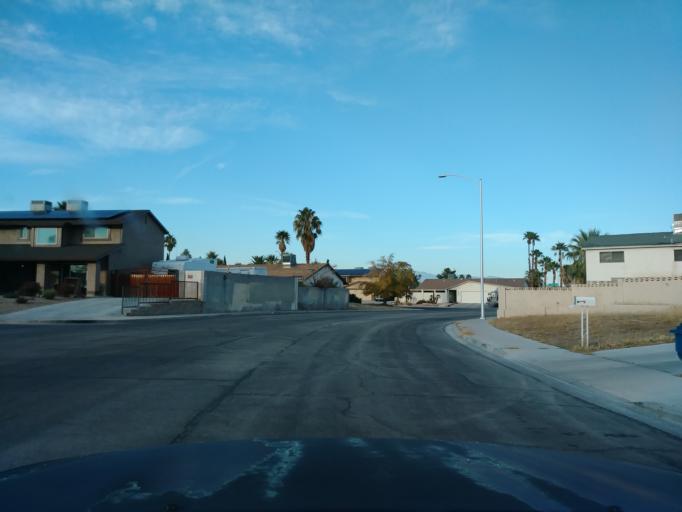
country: US
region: Nevada
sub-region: Clark County
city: Spring Valley
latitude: 36.1690
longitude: -115.2385
